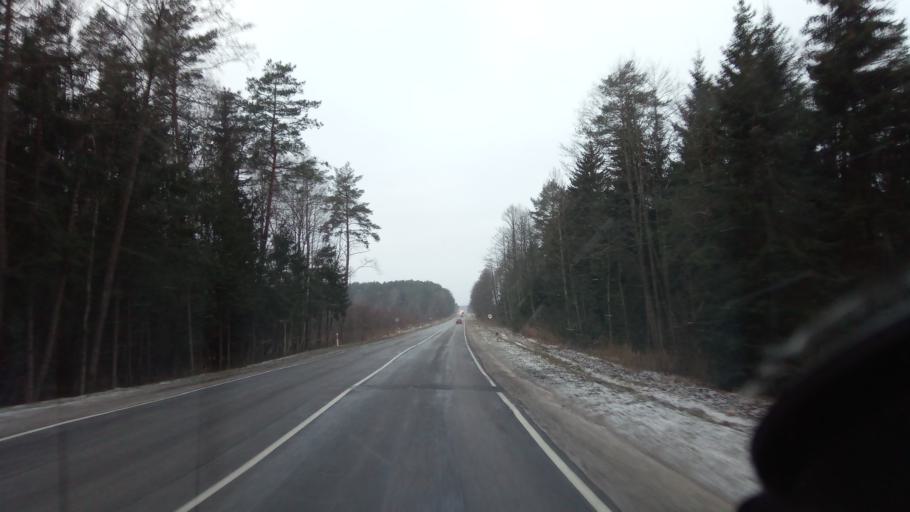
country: LT
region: Vilnius County
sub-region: Trakai
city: Rudiskes
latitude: 54.3743
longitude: 24.8979
